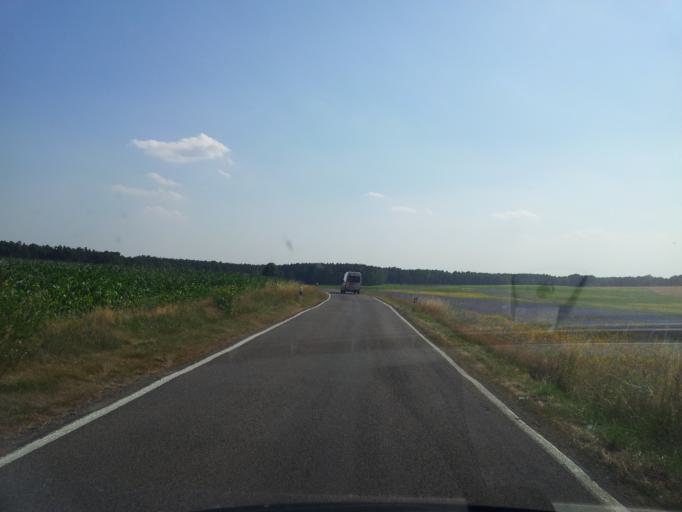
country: DE
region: Saxony
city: Hockendorf
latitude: 51.2194
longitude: 13.9108
